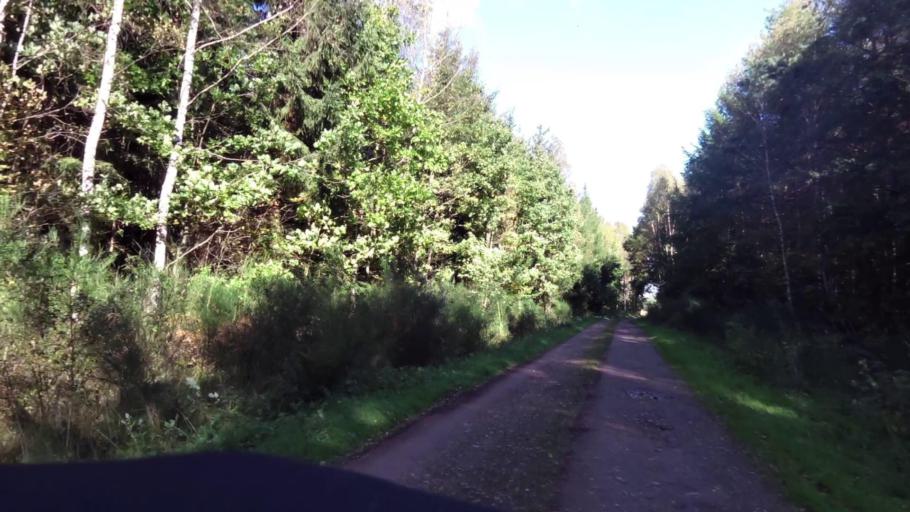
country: PL
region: West Pomeranian Voivodeship
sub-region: Powiat bialogardzki
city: Tychowo
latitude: 54.0113
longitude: 16.1372
